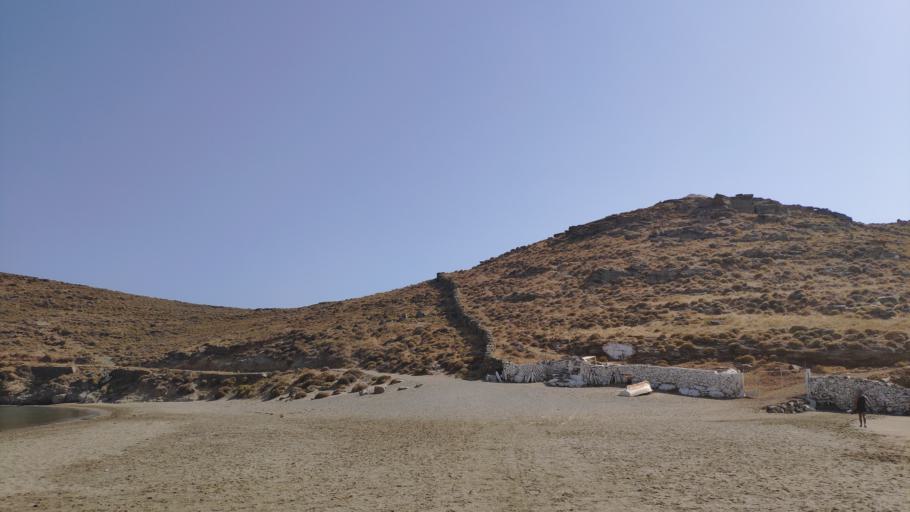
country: GR
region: South Aegean
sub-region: Nomos Kykladon
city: Kythnos
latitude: 37.4139
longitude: 24.3787
